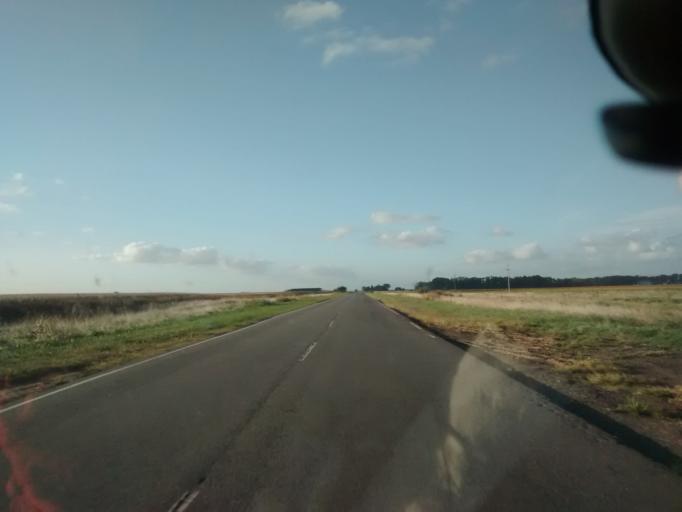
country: AR
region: Buenos Aires
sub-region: Partido de General Belgrano
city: General Belgrano
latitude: -36.0494
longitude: -58.6249
